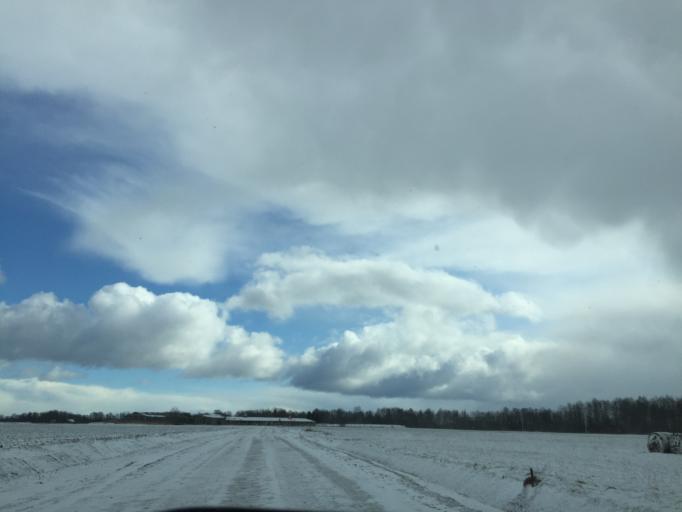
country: LV
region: Ventspils
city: Ventspils
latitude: 57.3724
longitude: 21.6253
